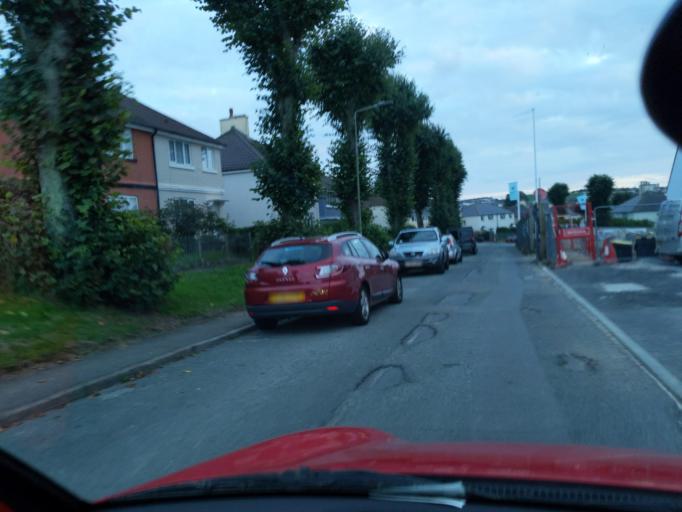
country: GB
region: England
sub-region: Cornwall
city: Millbrook
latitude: 50.3914
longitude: -4.1672
